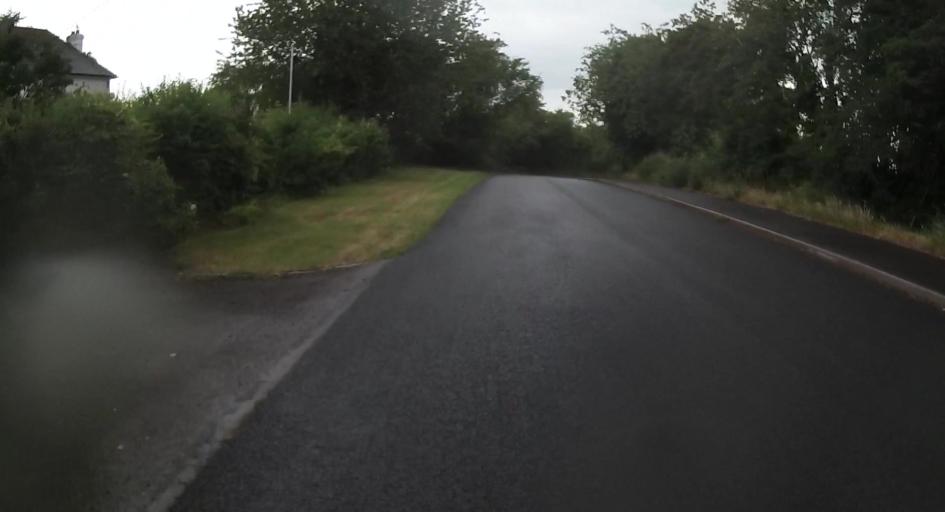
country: GB
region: England
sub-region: Hampshire
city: Odiham
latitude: 51.2485
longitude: -0.9519
